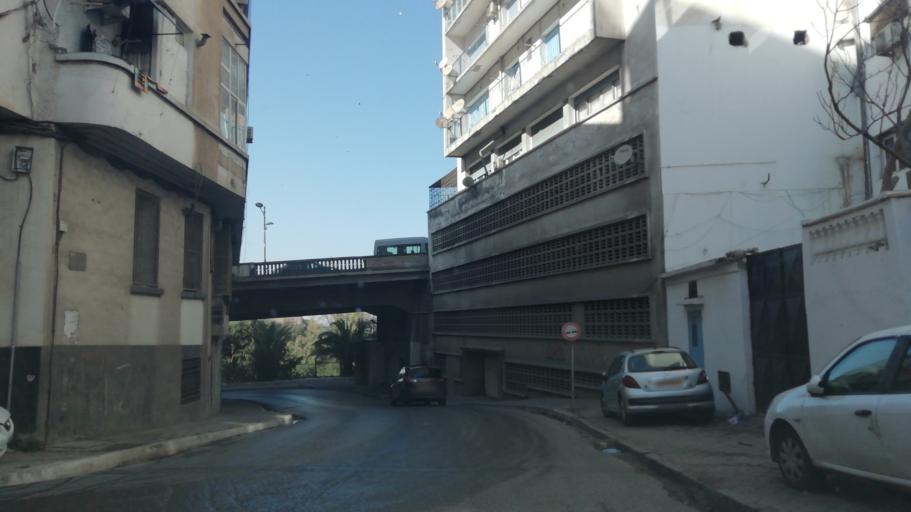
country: DZ
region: Oran
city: Oran
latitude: 35.7051
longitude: -0.6407
